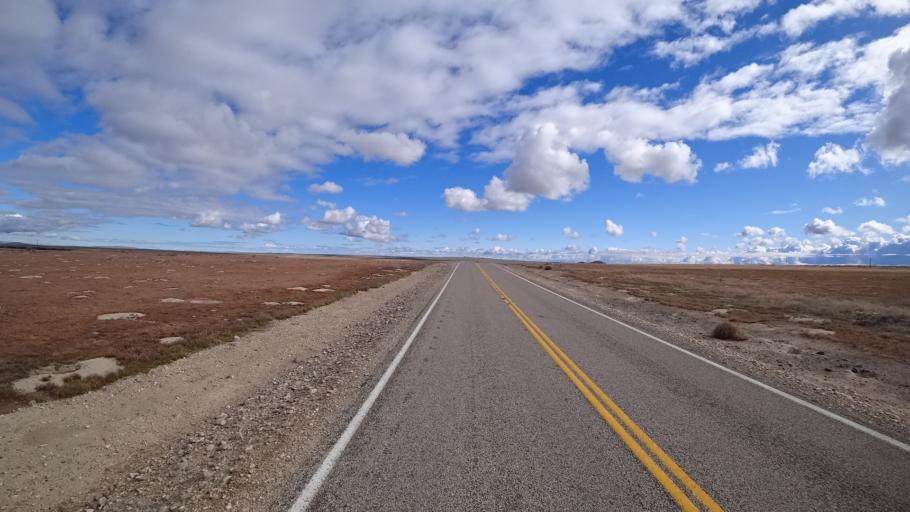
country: US
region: Idaho
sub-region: Owyhee County
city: Murphy
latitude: 43.2811
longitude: -116.3939
